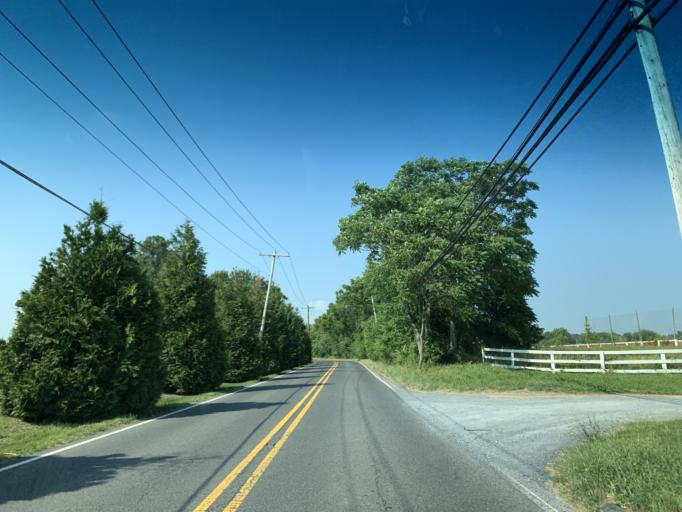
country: US
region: Maryland
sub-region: Montgomery County
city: Poolesville
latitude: 39.1630
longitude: -77.4185
